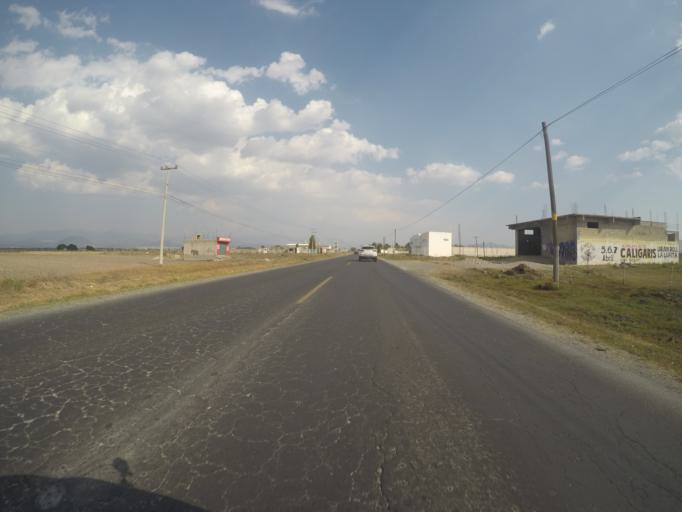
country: MX
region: Morelos
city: Chapultepec
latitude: 19.1952
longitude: -99.5405
